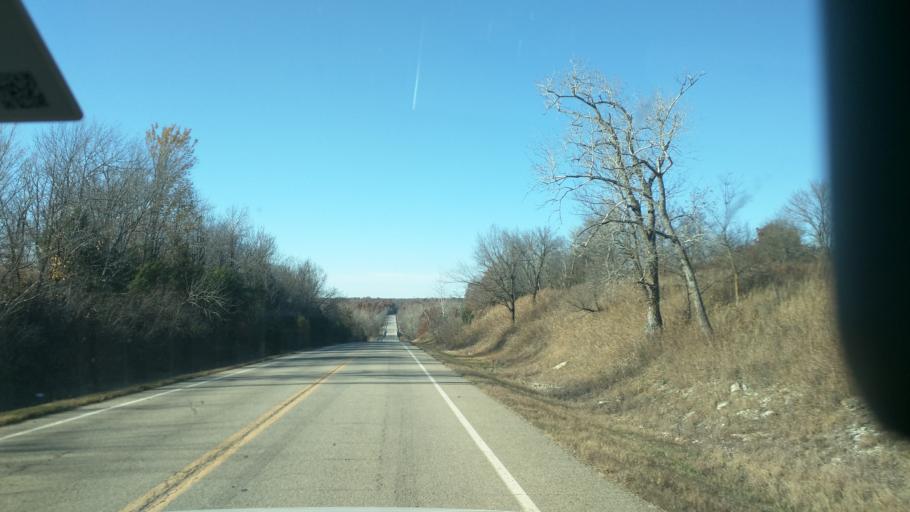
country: US
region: Oklahoma
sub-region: Nowata County
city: Nowata
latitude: 36.7449
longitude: -95.5263
